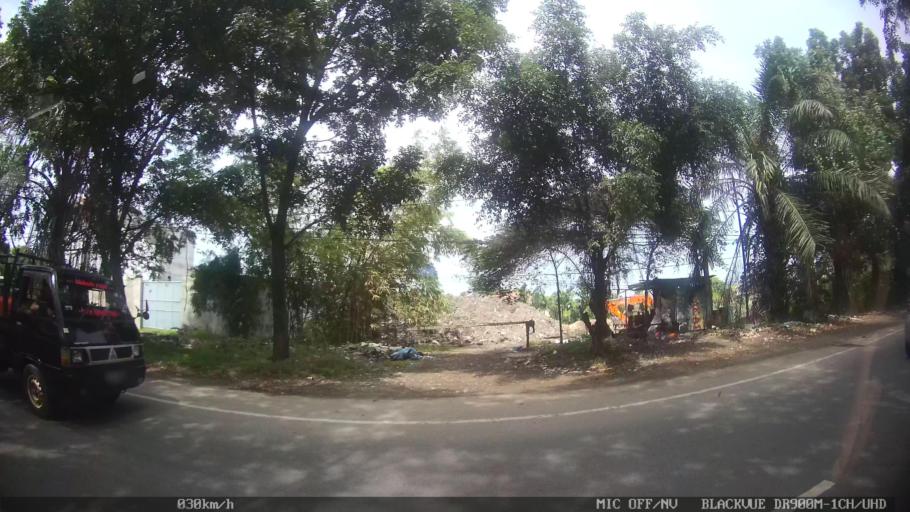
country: ID
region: North Sumatra
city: Sunggal
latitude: 3.6079
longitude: 98.6277
